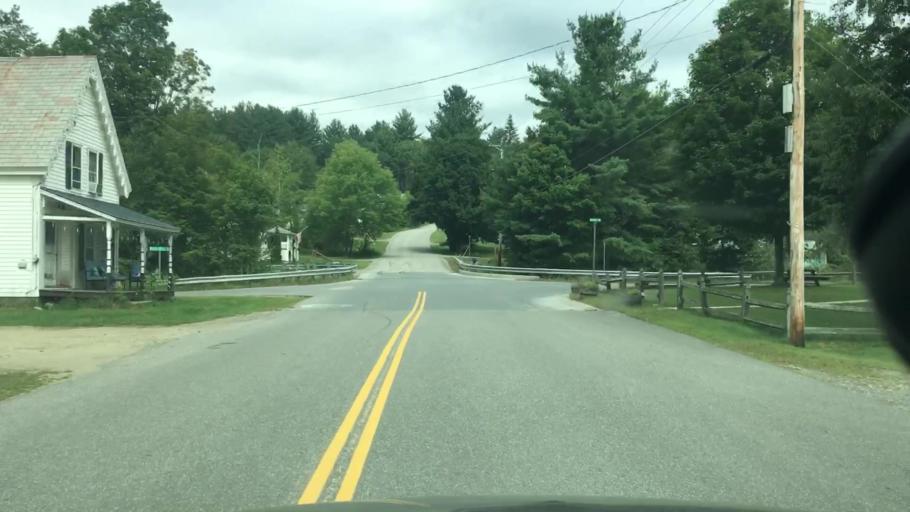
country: US
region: Massachusetts
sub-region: Franklin County
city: Colrain
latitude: 42.7870
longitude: -72.7708
